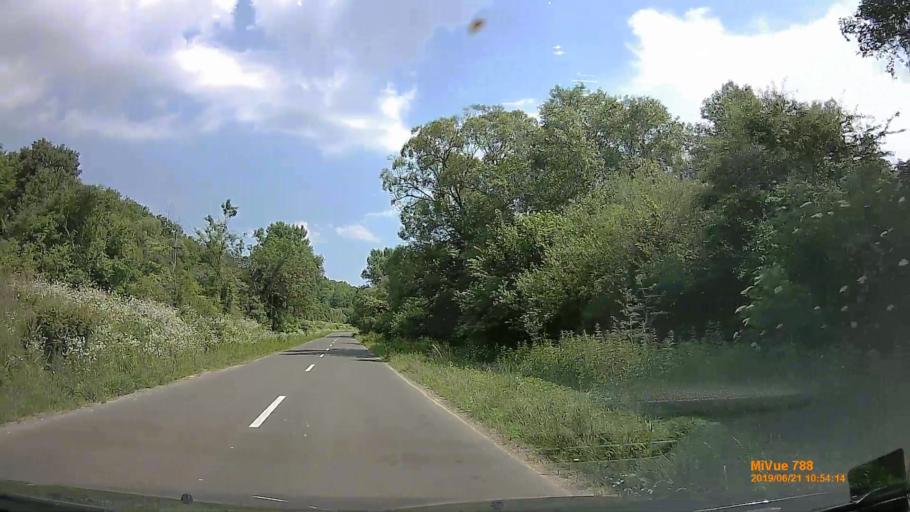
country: HU
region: Baranya
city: Buekkoesd
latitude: 46.1513
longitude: 18.0642
